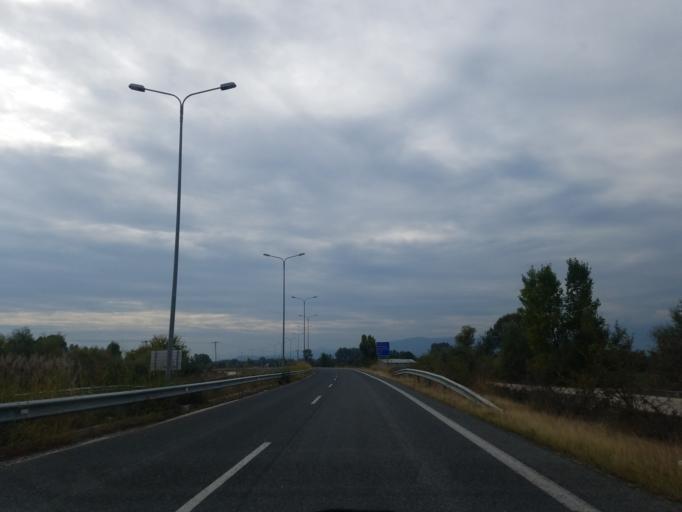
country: GR
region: Thessaly
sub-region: Trikala
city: Pyrgetos
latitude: 39.5394
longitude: 21.7358
